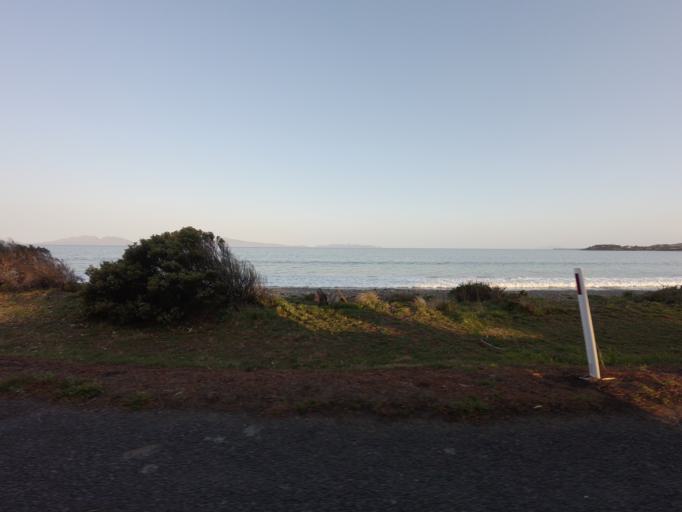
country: AU
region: Tasmania
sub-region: Break O'Day
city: St Helens
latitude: -42.1278
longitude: 148.0818
